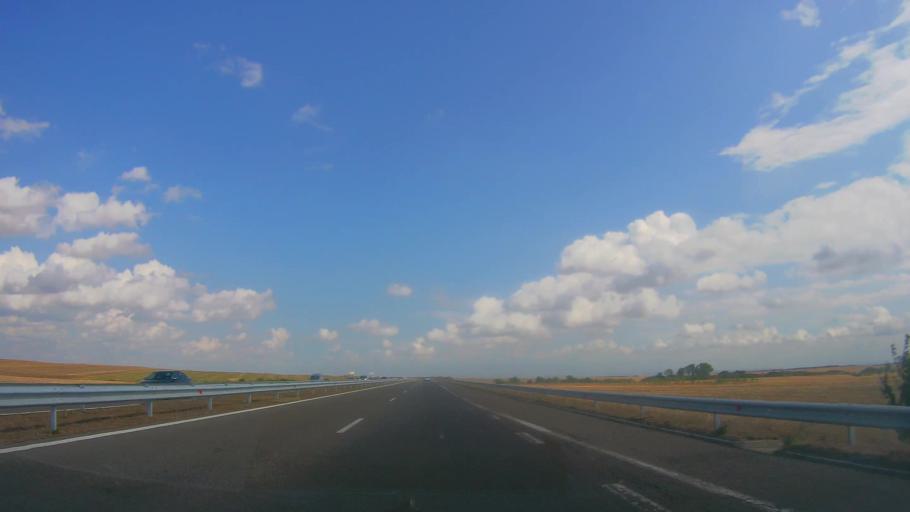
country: BG
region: Burgas
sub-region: Obshtina Karnobat
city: Karnobat
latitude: 42.5862
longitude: 27.1270
